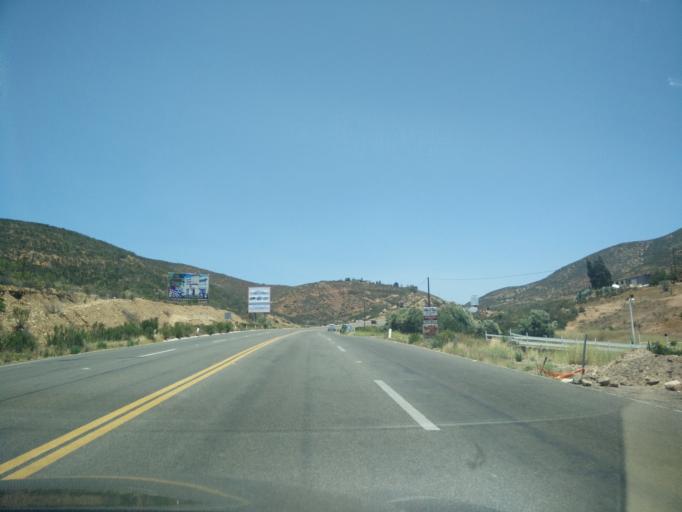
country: MX
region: Baja California
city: El Sauzal
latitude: 31.9501
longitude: -116.6662
